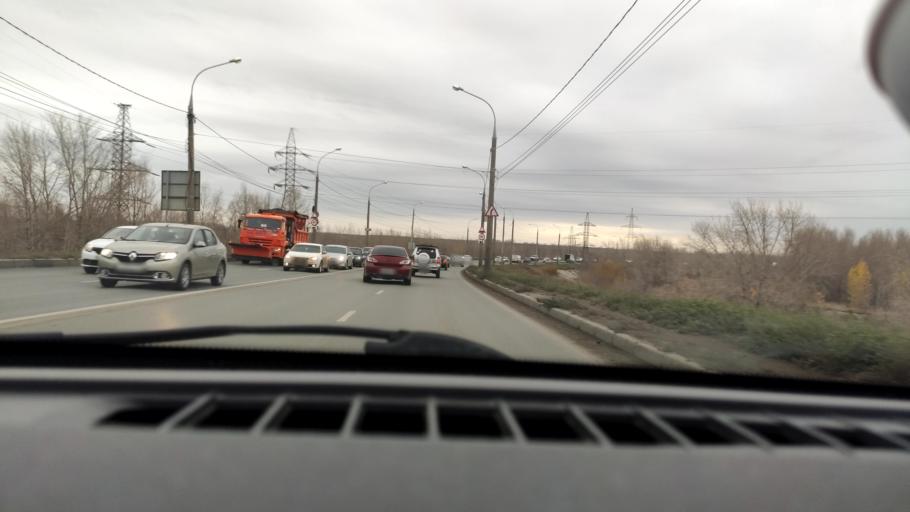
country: RU
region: Samara
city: Samara
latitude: 53.1668
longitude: 50.1966
